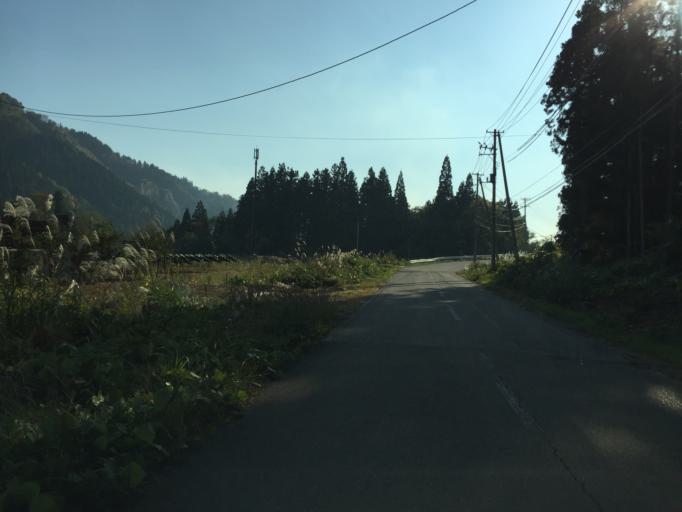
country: JP
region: Fukushima
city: Kitakata
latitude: 37.7479
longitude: 139.8975
